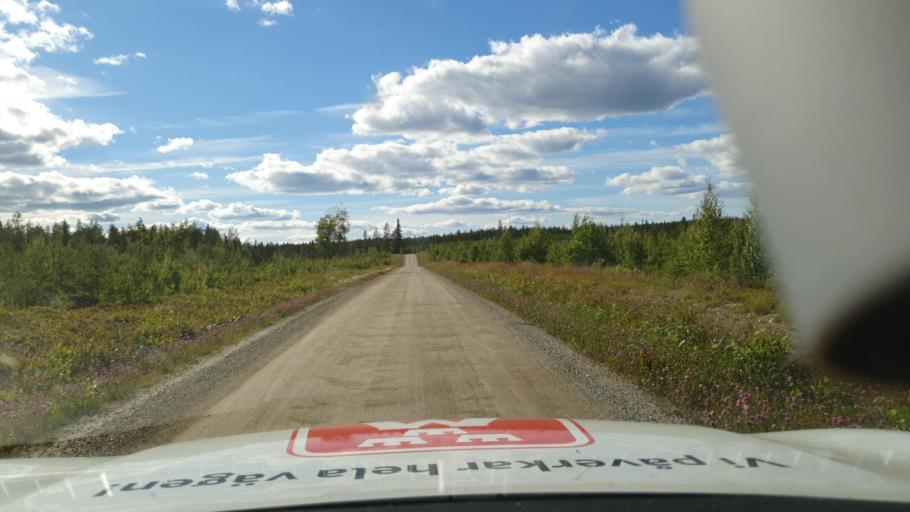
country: SE
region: Vaesterbotten
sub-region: Lycksele Kommun
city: Lycksele
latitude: 64.4026
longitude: 18.5612
